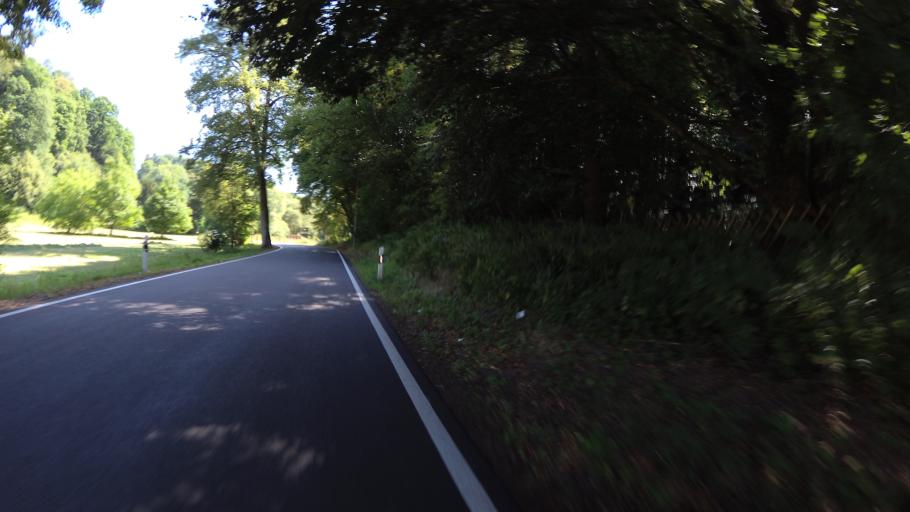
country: DE
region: Rheinland-Pfalz
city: Zweibrucken
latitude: 49.2433
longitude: 7.3153
